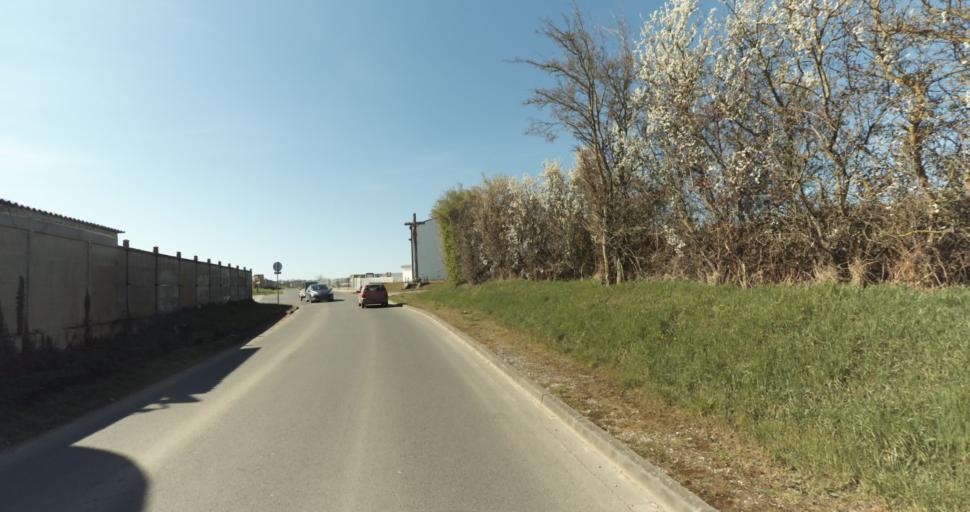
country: FR
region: Lower Normandy
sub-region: Departement du Calvados
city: Saint-Pierre-sur-Dives
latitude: 49.0249
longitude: -0.0425
